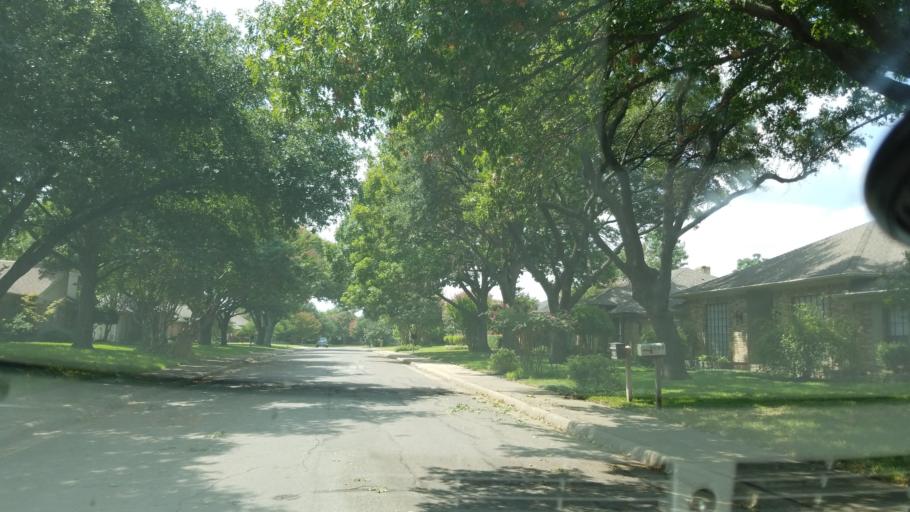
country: US
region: Texas
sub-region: Dallas County
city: Richardson
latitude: 32.9190
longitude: -96.7199
